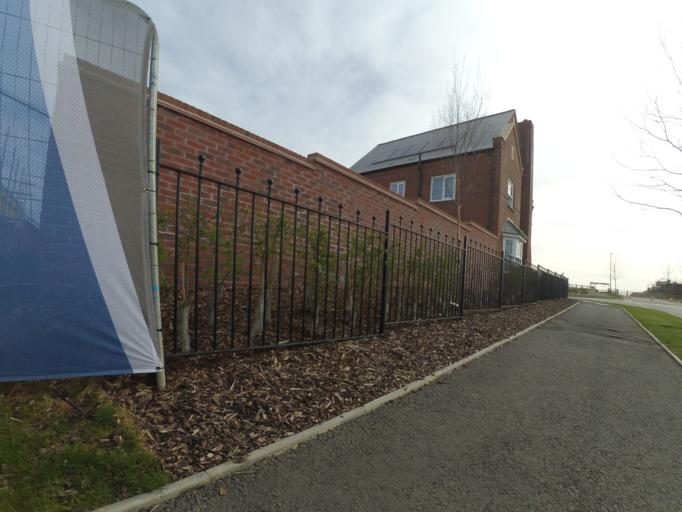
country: GB
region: England
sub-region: Warwickshire
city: Rugby
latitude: 52.3604
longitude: -1.1928
